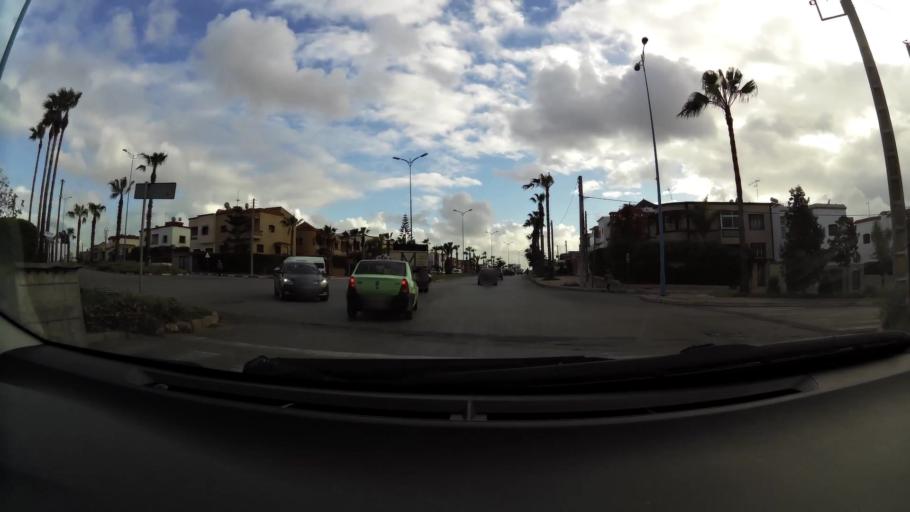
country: MA
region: Grand Casablanca
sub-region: Mohammedia
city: Mohammedia
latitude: 33.6965
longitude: -7.3718
